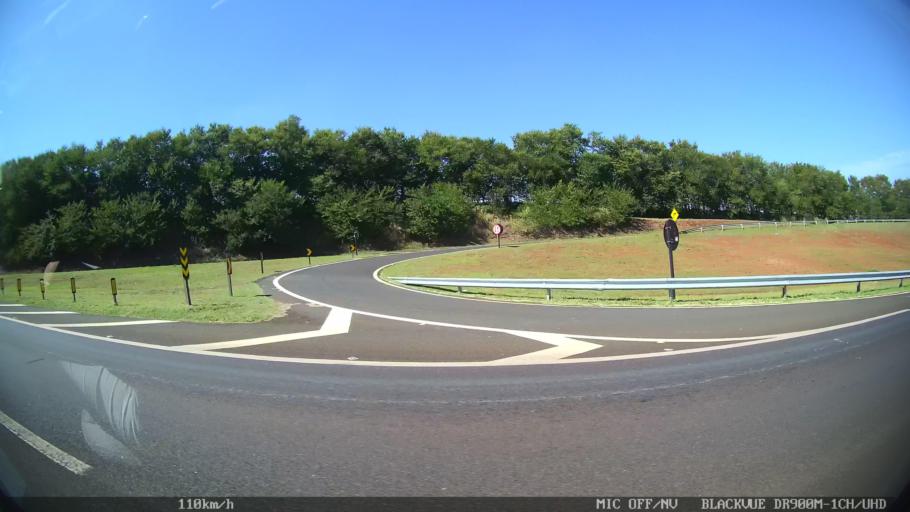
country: BR
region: Sao Paulo
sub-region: Franca
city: Franca
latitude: -20.5901
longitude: -47.4377
